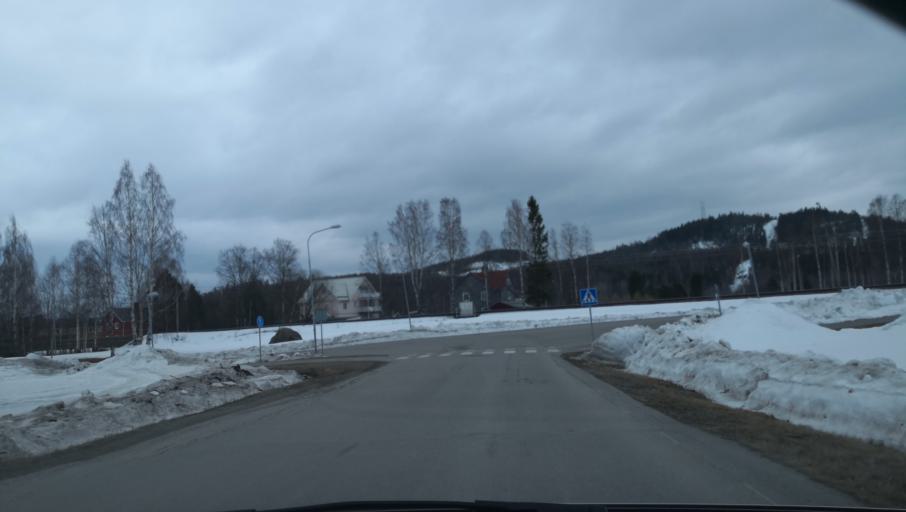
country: SE
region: Vaesterbotten
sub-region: Vannas Kommun
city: Vannasby
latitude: 63.9160
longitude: 19.8110
